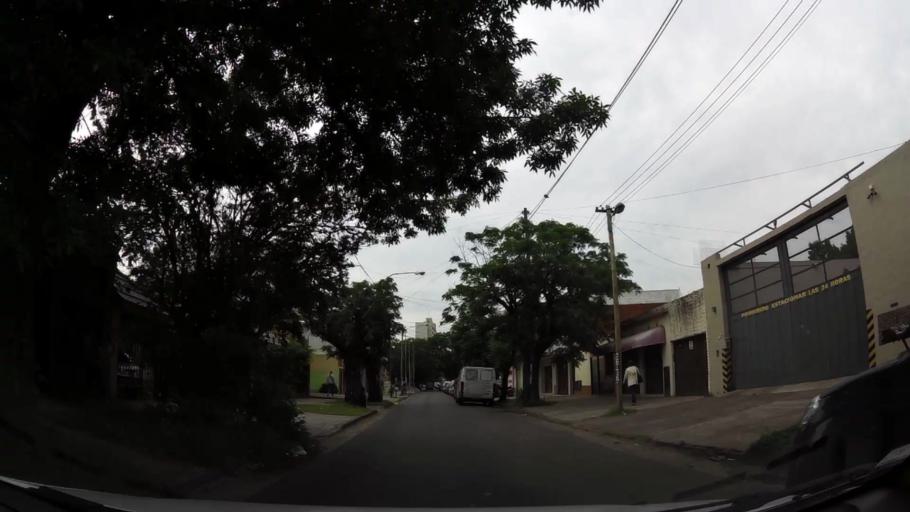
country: AR
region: Buenos Aires F.D.
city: Villa Lugano
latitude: -34.7049
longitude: -58.5053
